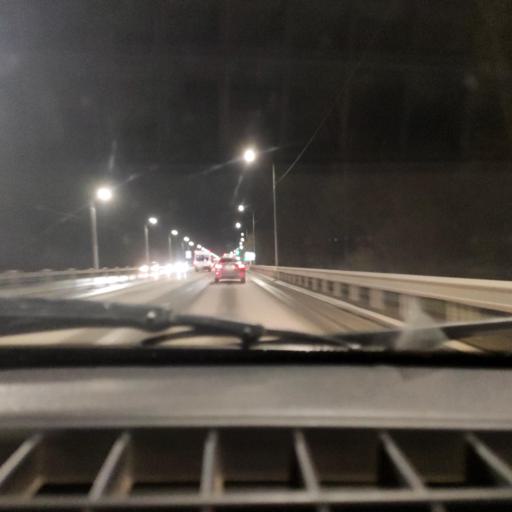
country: RU
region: Bashkortostan
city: Ufa
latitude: 54.7008
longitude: 55.9345
